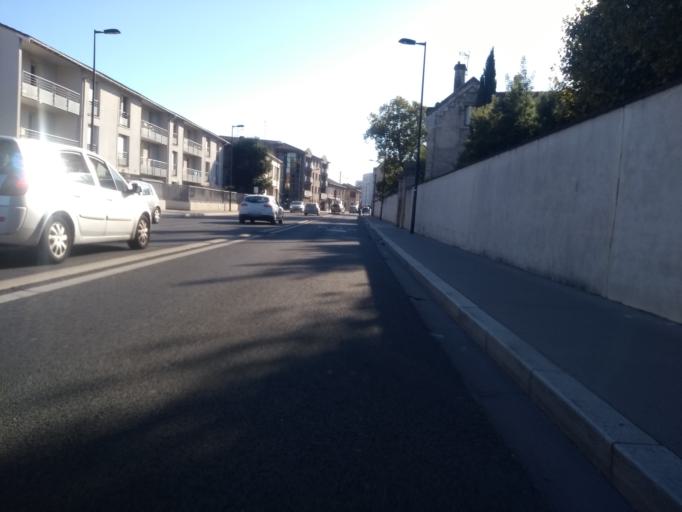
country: FR
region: Aquitaine
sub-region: Departement de la Gironde
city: Talence
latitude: 44.8245
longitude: -0.5994
